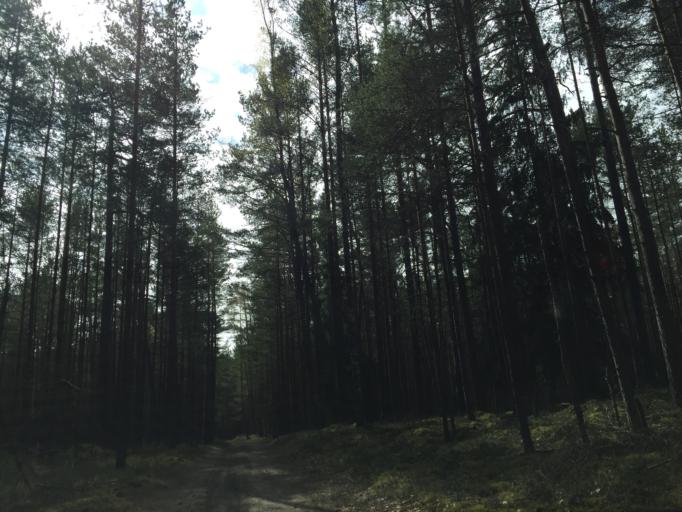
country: LV
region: Salacgrivas
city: Salacgriva
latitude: 57.6911
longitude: 24.3607
